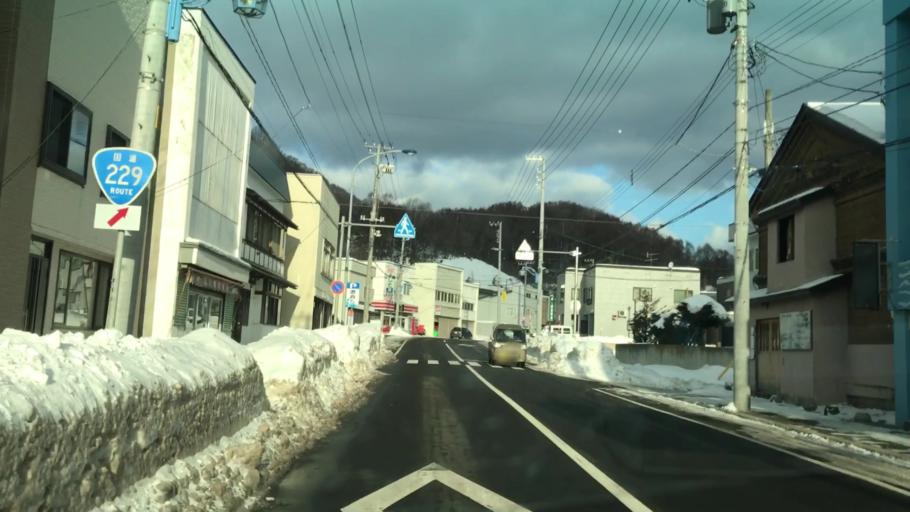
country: JP
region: Hokkaido
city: Yoichi
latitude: 43.2779
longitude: 140.6384
